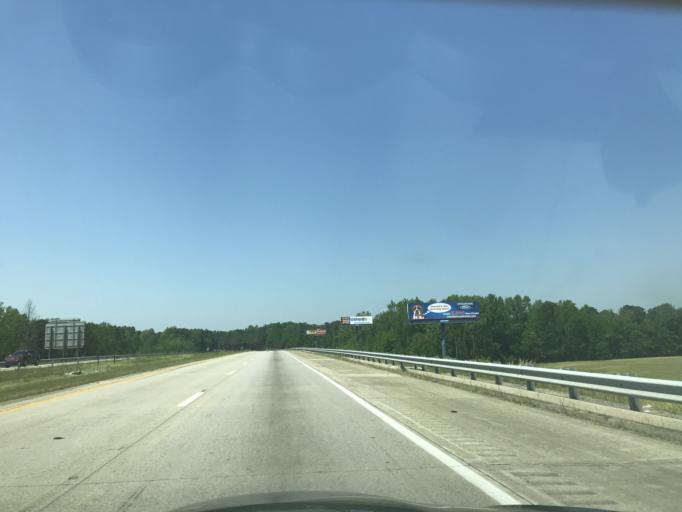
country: US
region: North Carolina
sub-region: Johnston County
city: Benson
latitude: 35.4076
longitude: -78.5239
